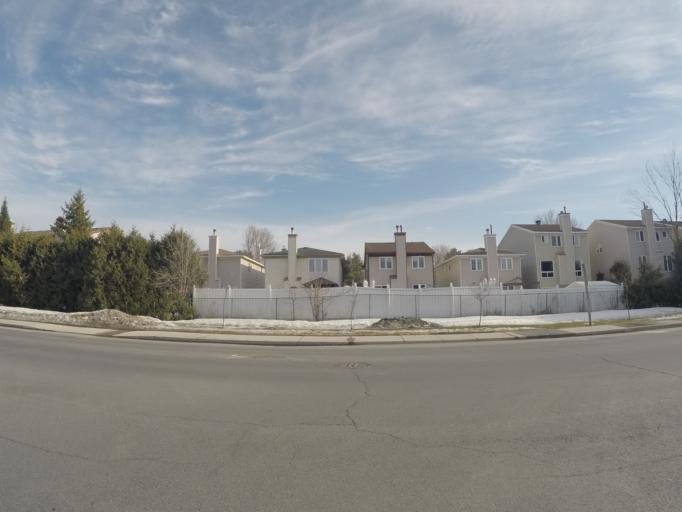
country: CA
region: Quebec
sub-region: Outaouais
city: Gatineau
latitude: 45.4633
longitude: -75.5013
